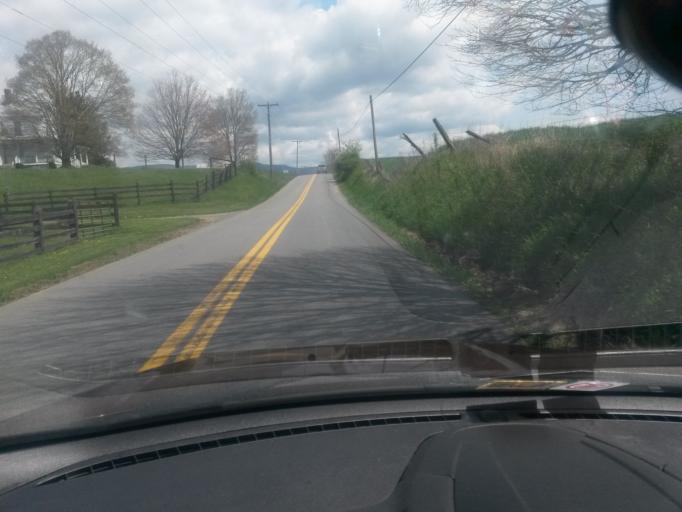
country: US
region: West Virginia
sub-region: Pocahontas County
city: Marlinton
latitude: 38.1249
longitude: -80.2137
